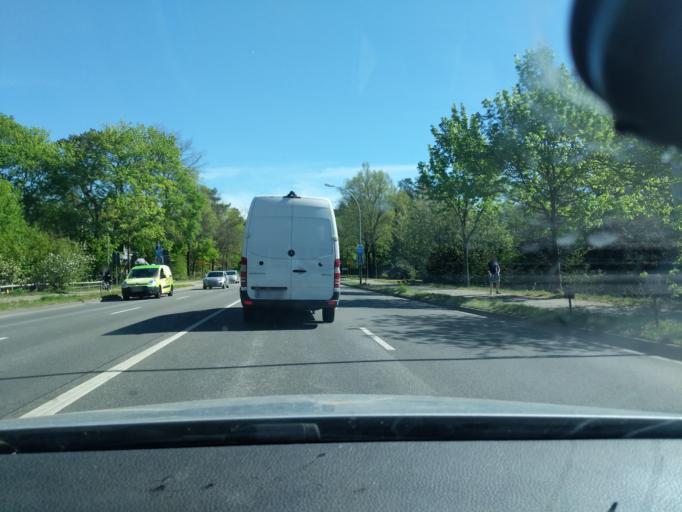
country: DE
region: Lower Saxony
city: Neu Wulmstorf
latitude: 53.4662
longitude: 9.8061
